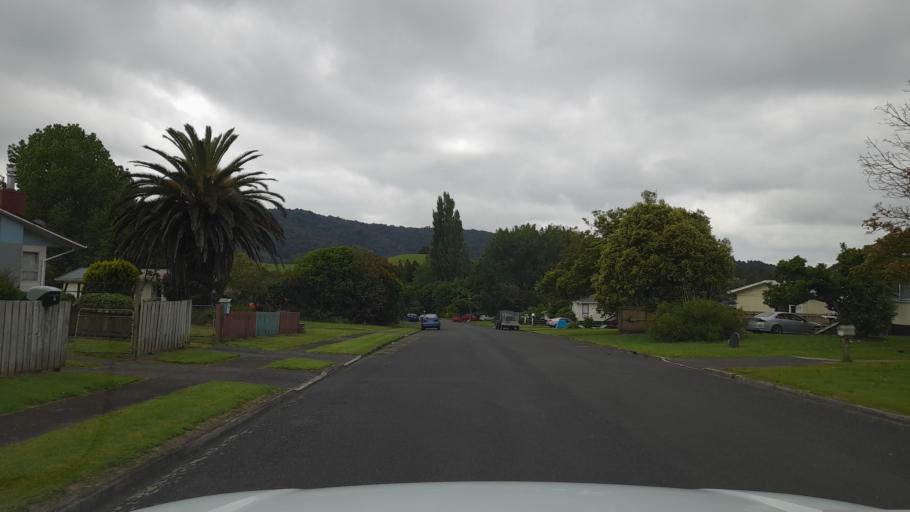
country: NZ
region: Northland
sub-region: Far North District
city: Waimate North
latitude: -35.4023
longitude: 173.7904
